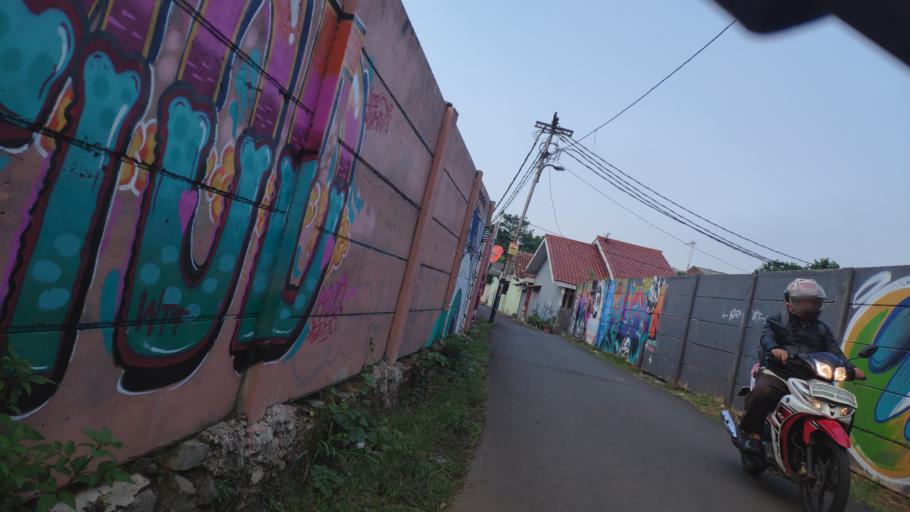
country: ID
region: Jakarta Raya
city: Jakarta
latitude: -6.2911
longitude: 106.8153
